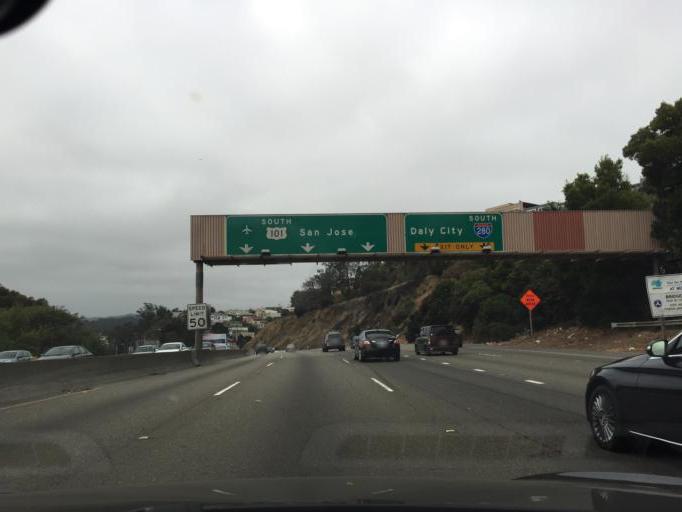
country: US
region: California
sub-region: San Francisco County
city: San Francisco
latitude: 37.7429
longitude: -122.4067
